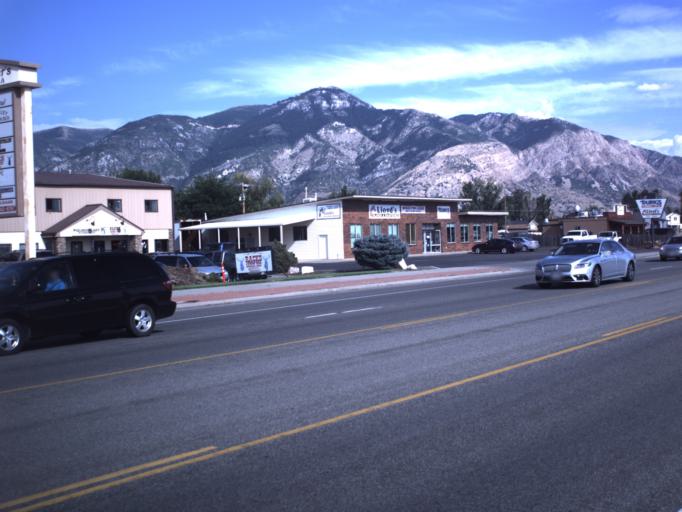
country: US
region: Utah
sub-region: Weber County
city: Harrisville
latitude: 41.2983
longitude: -111.9980
